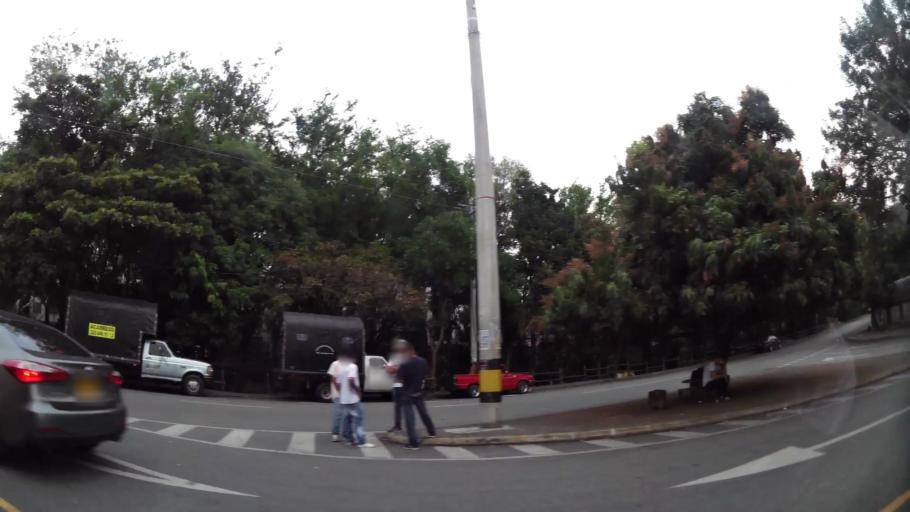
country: CO
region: Antioquia
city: Medellin
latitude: 6.2513
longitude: -75.5996
